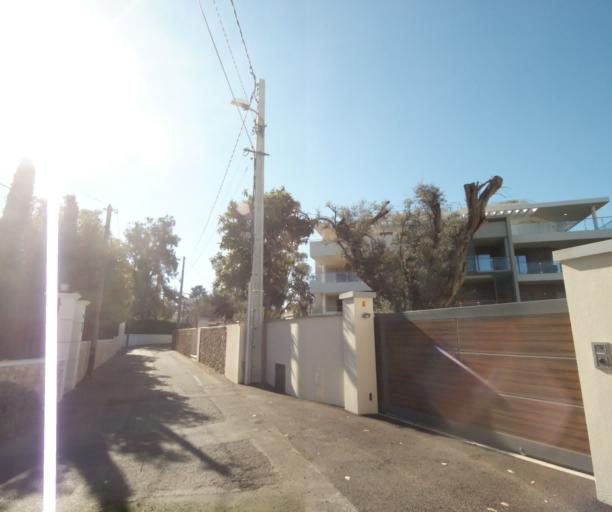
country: FR
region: Provence-Alpes-Cote d'Azur
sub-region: Departement des Alpes-Maritimes
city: Antibes
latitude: 43.5654
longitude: 7.1201
